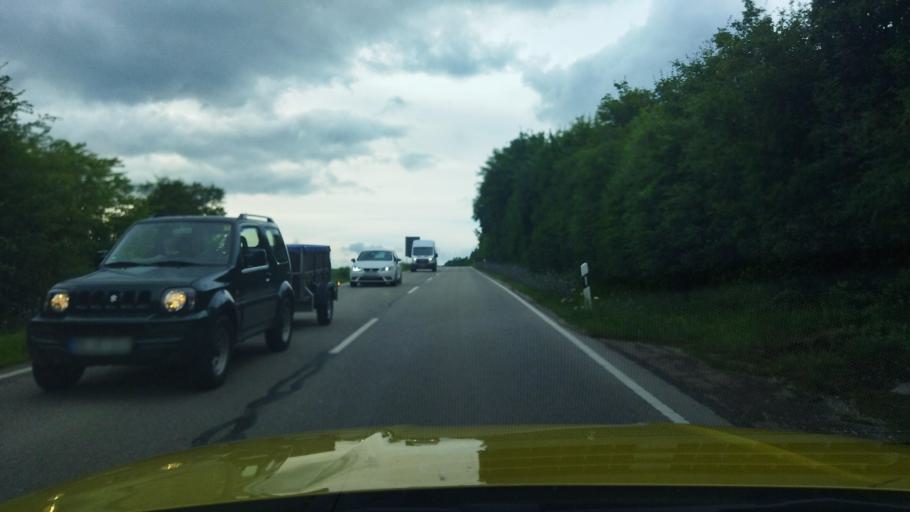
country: DE
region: Bavaria
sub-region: Regierungsbezirk Mittelfranken
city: Greding
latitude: 49.0472
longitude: 11.3468
